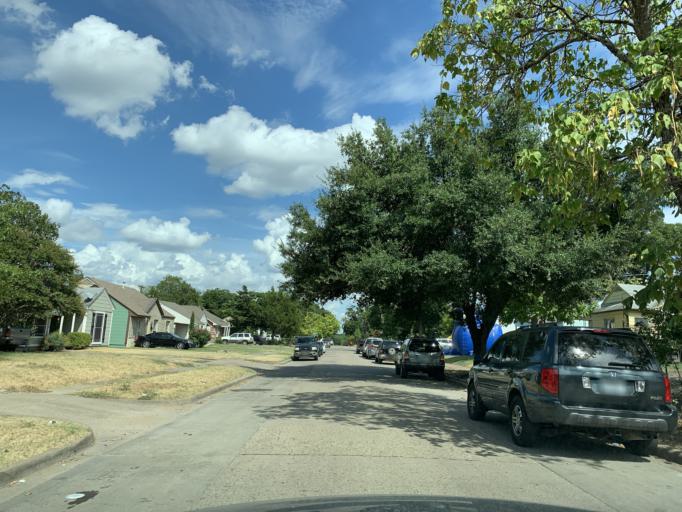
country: US
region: Texas
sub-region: Dallas County
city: Cockrell Hill
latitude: 32.7363
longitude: -96.8726
